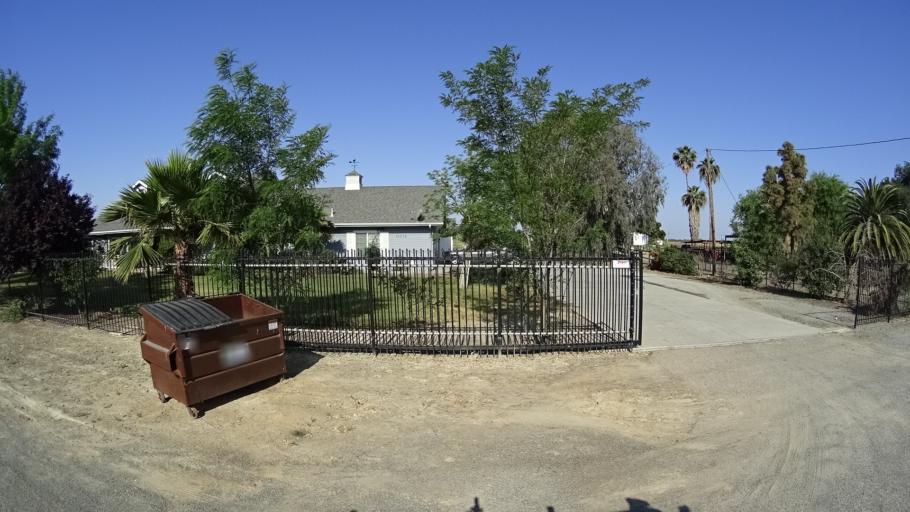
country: US
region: California
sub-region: Kings County
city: Home Garden
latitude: 36.3171
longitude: -119.5831
